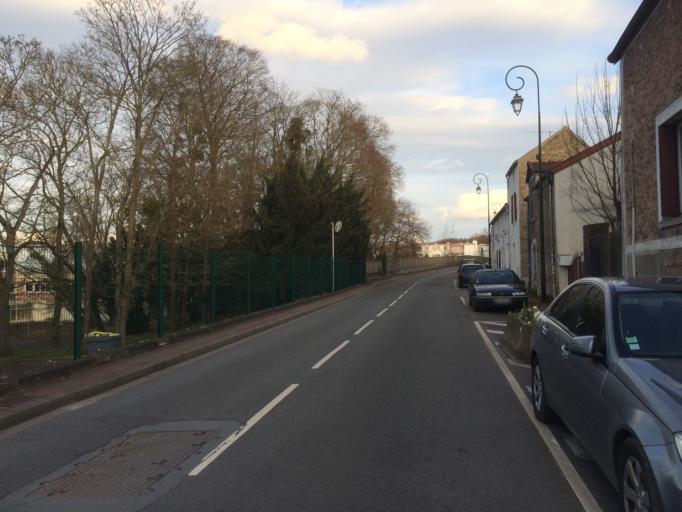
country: FR
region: Ile-de-France
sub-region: Departement de l'Essonne
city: Villebon-sur-Yvette
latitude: 48.6999
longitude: 2.2232
